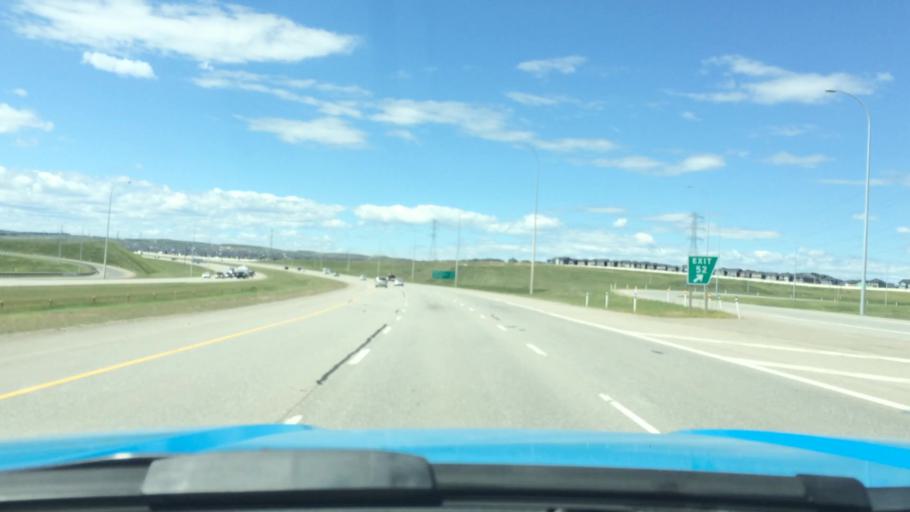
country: CA
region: Alberta
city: Calgary
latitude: 51.1750
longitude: -114.0864
